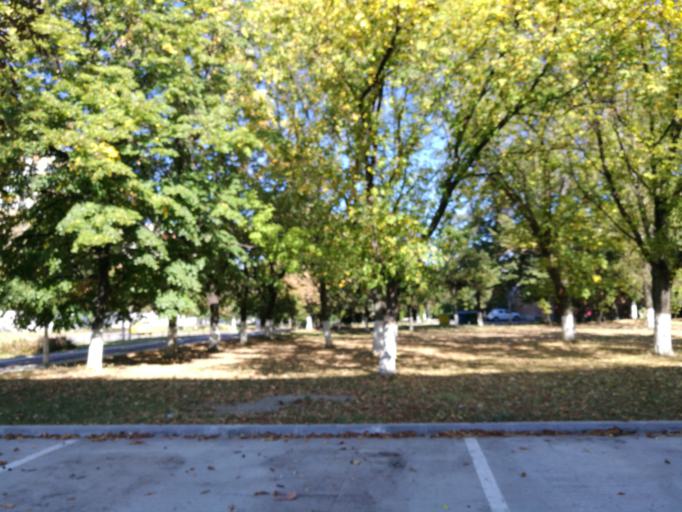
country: RO
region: Ilfov
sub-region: Comuna Chiajna
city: Rosu
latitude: 44.4354
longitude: 26.0454
